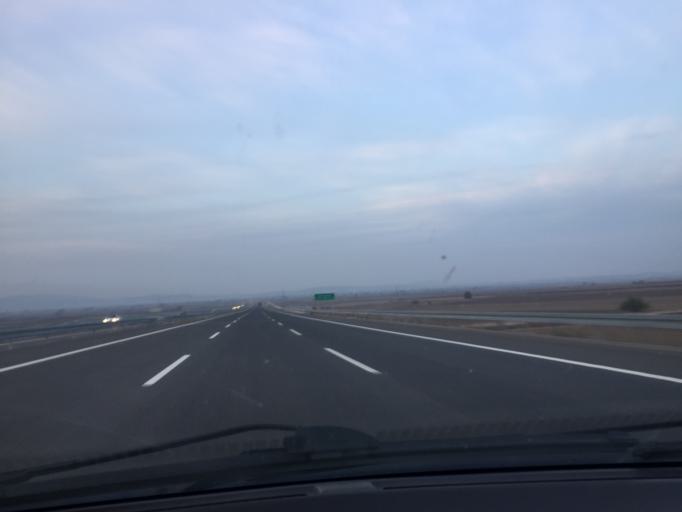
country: TR
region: Manisa
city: Halitpasa
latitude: 38.7051
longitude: 27.6450
